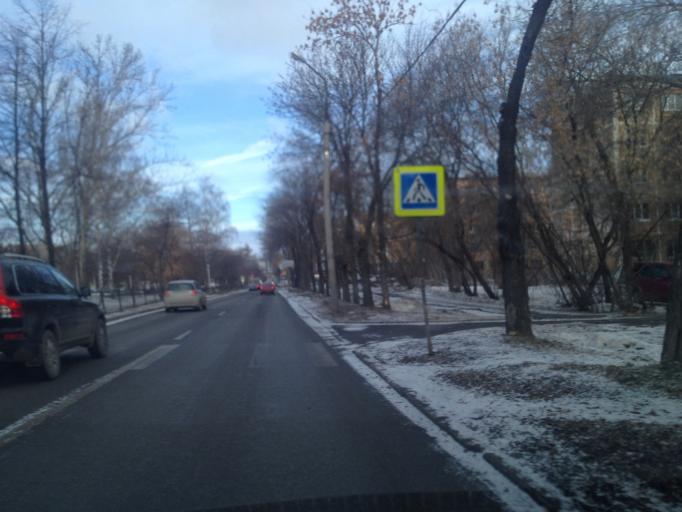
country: RU
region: Sverdlovsk
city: Yekaterinburg
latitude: 56.8200
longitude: 60.5789
